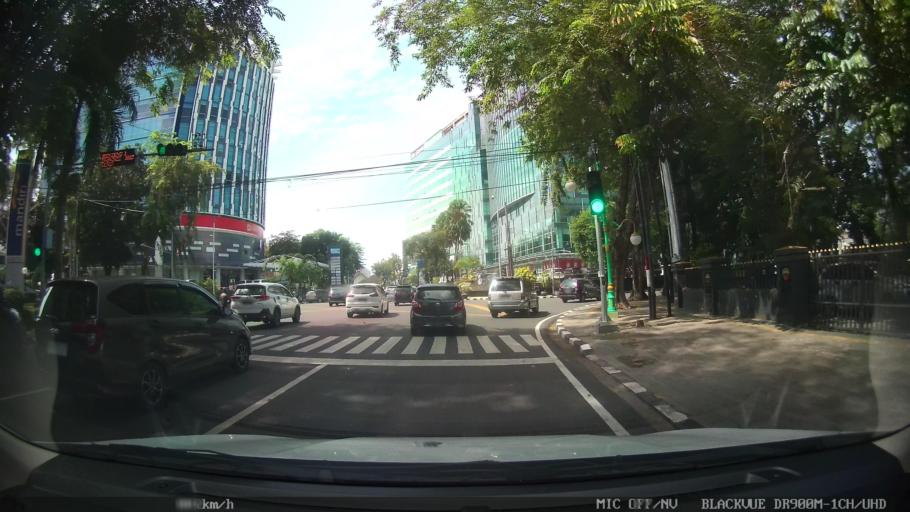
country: ID
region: North Sumatra
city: Medan
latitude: 3.5873
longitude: 98.6738
